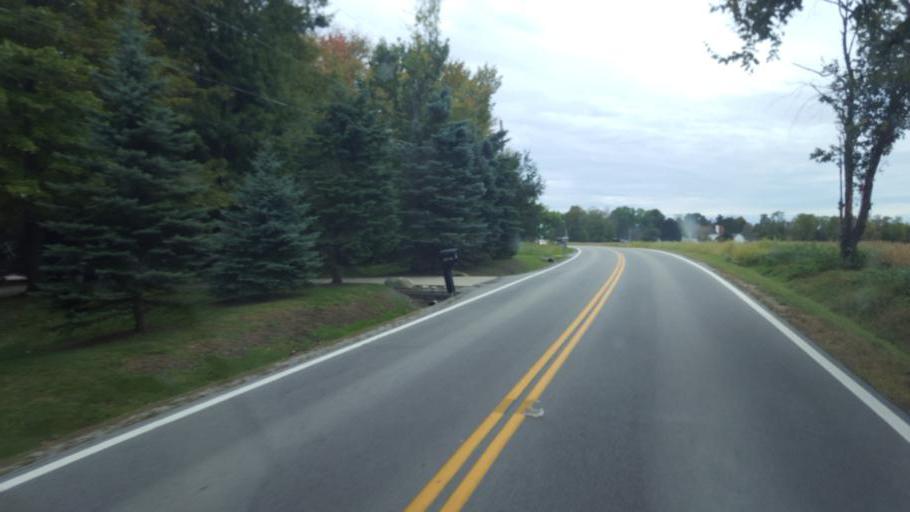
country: US
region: Ohio
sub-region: Huron County
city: Wakeman
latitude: 41.3087
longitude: -82.3668
